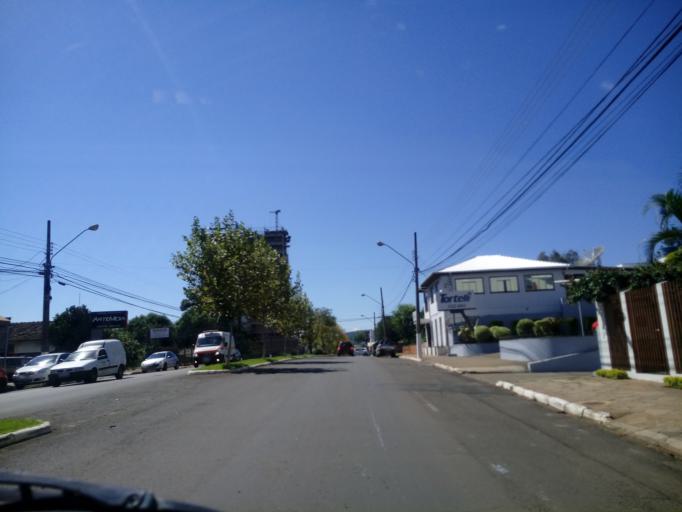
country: BR
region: Santa Catarina
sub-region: Chapeco
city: Chapeco
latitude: -27.0987
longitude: -52.6073
